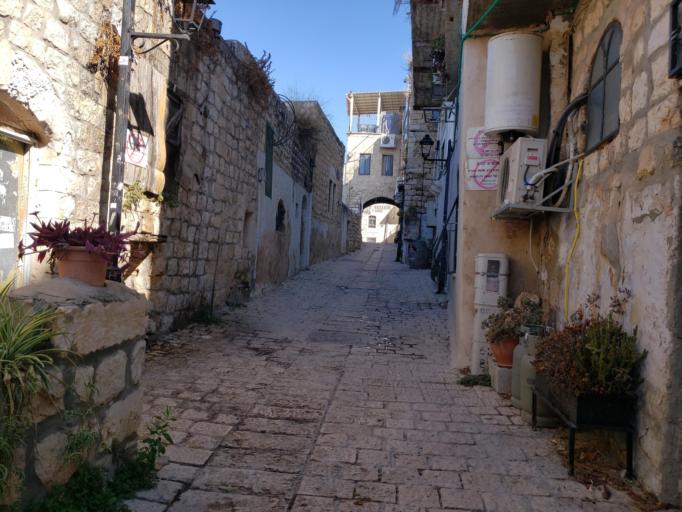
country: IL
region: Northern District
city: Safed
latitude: 32.9677
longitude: 35.4919
